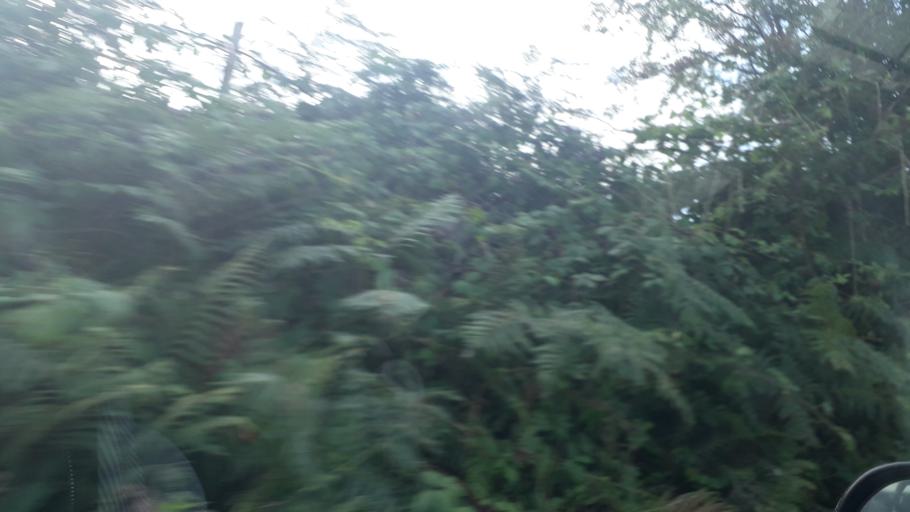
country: GB
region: Northern Ireland
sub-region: Down District
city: Warrenpoint
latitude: 54.0685
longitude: -6.2780
